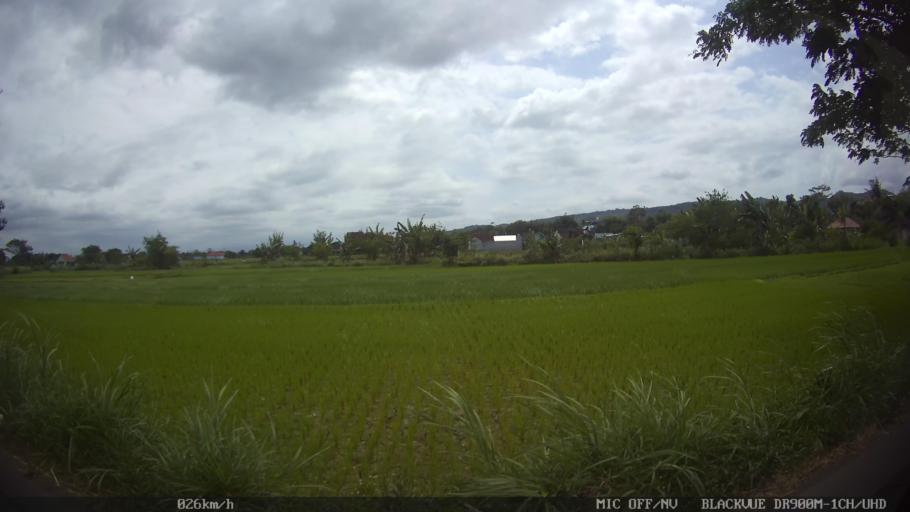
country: ID
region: Central Java
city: Candi Prambanan
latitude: -7.8138
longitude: 110.4953
